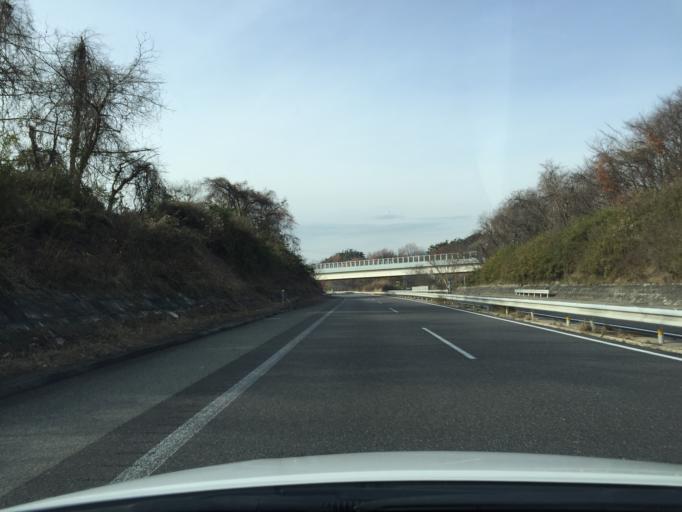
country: JP
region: Fukushima
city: Miharu
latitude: 37.4365
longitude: 140.4559
